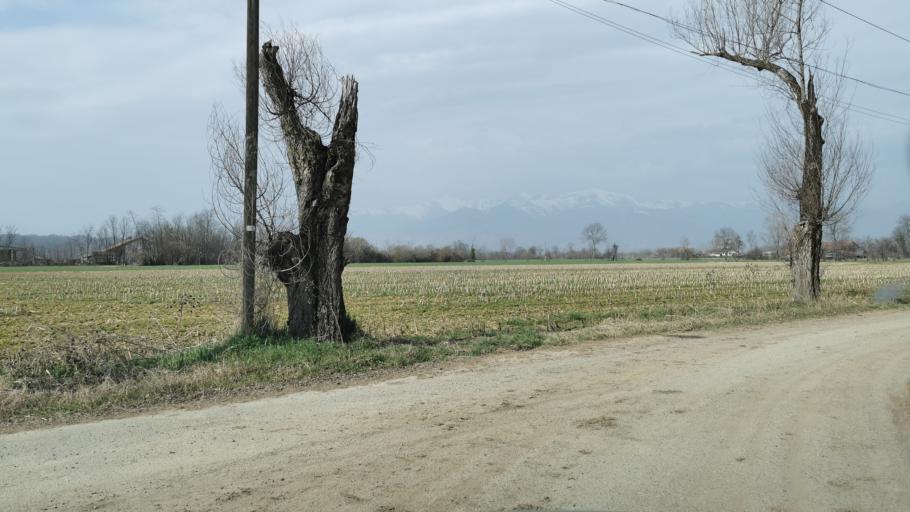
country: IT
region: Piedmont
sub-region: Provincia di Torino
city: Front
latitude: 45.2835
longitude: 7.6947
